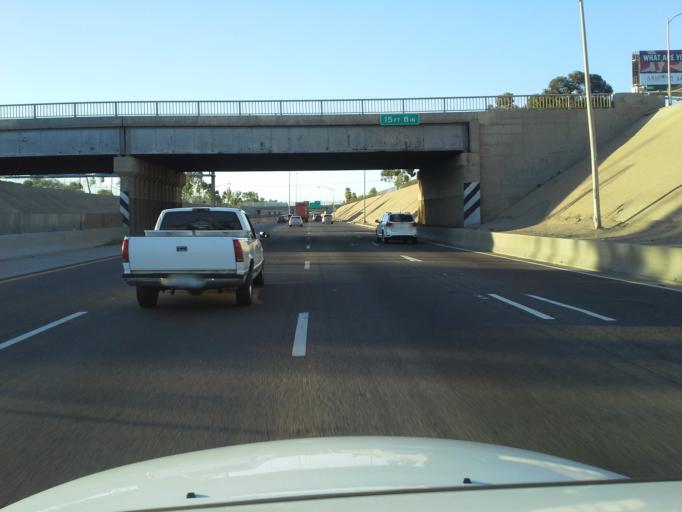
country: US
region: Arizona
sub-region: Maricopa County
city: Phoenix
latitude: 33.4434
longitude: -112.1081
